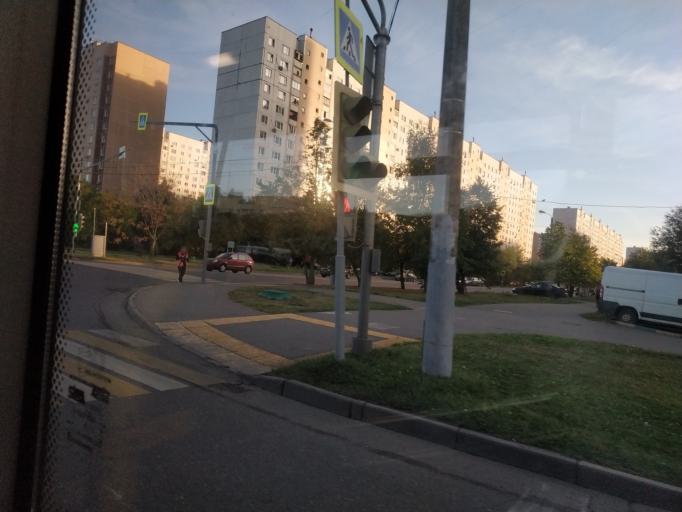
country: RU
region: Moscow
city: Novo-Peredelkino
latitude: 55.6454
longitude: 37.3517
